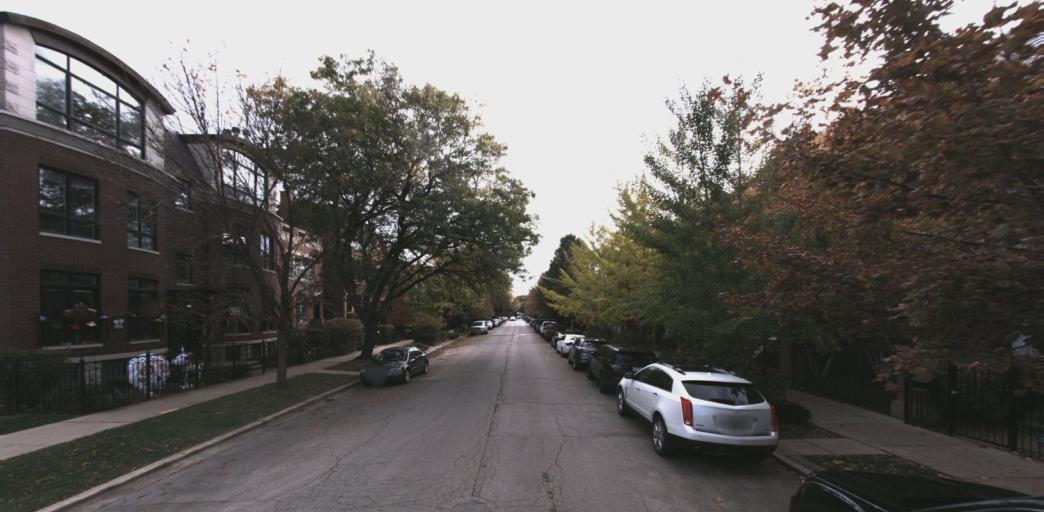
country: US
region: Illinois
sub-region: Cook County
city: Chicago
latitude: 41.9309
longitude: -87.6708
